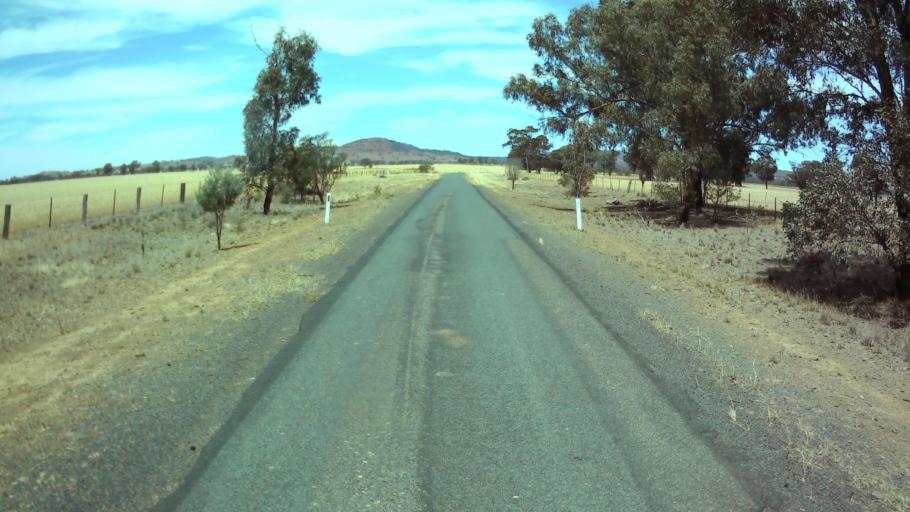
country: AU
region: New South Wales
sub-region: Weddin
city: Grenfell
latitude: -33.7569
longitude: 148.0957
